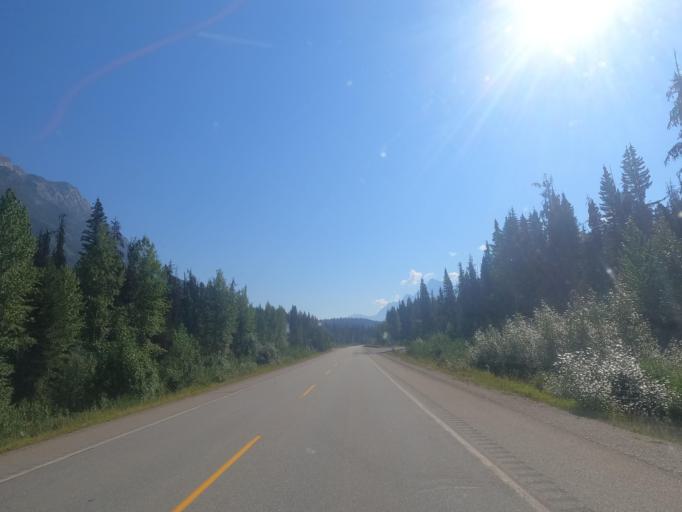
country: CA
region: Alberta
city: Jasper Park Lodge
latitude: 52.8630
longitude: -118.6521
